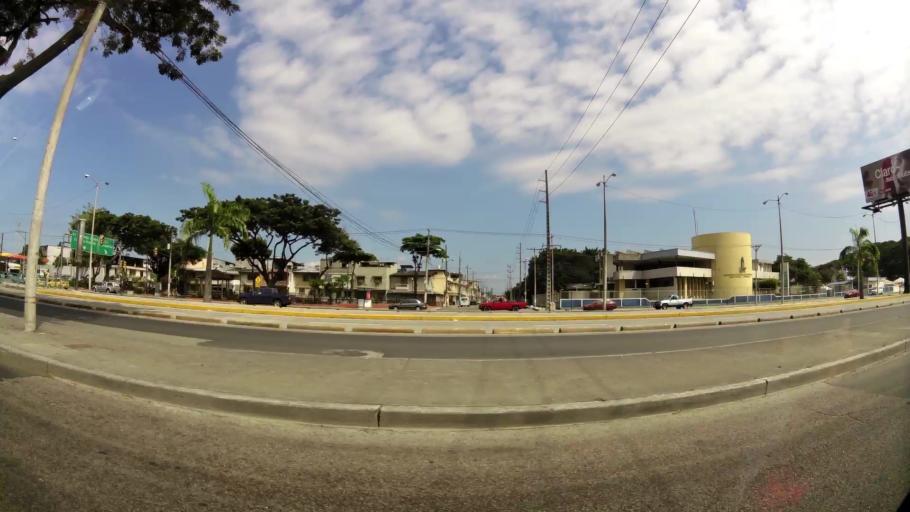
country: EC
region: Guayas
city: Guayaquil
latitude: -2.2357
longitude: -79.8966
